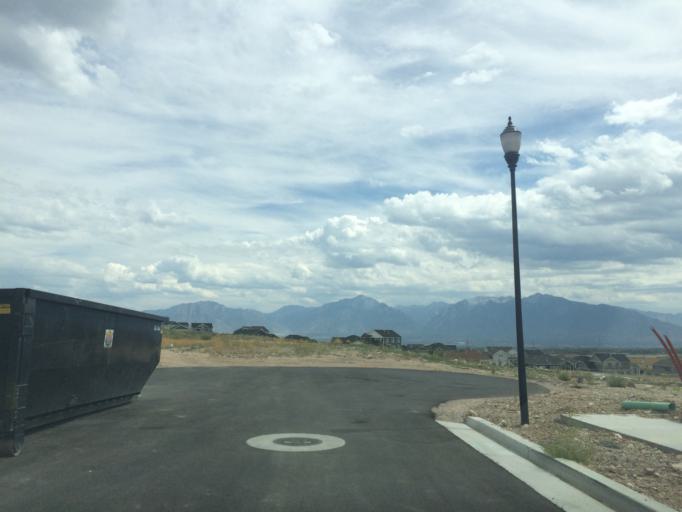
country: US
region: Utah
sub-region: Salt Lake County
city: Oquirrh
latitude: 40.6121
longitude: -112.0499
